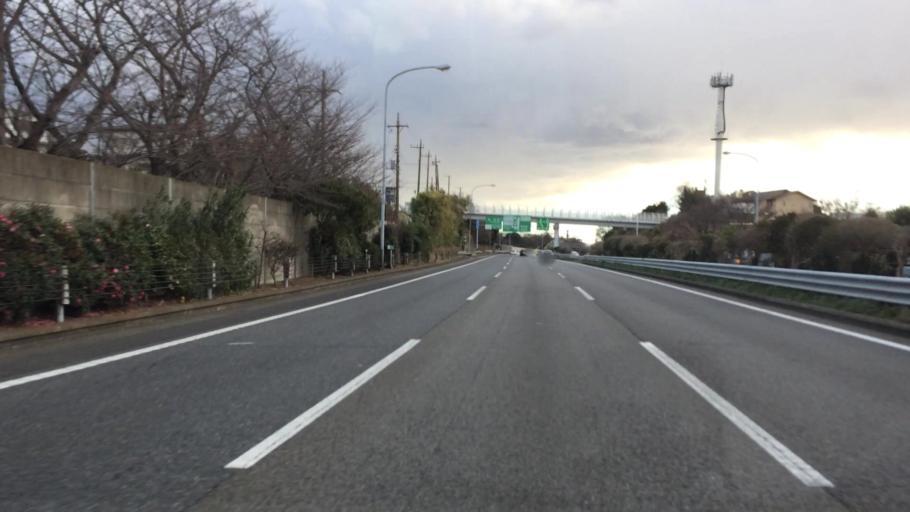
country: JP
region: Kanagawa
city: Yokohama
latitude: 35.4961
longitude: 139.5916
